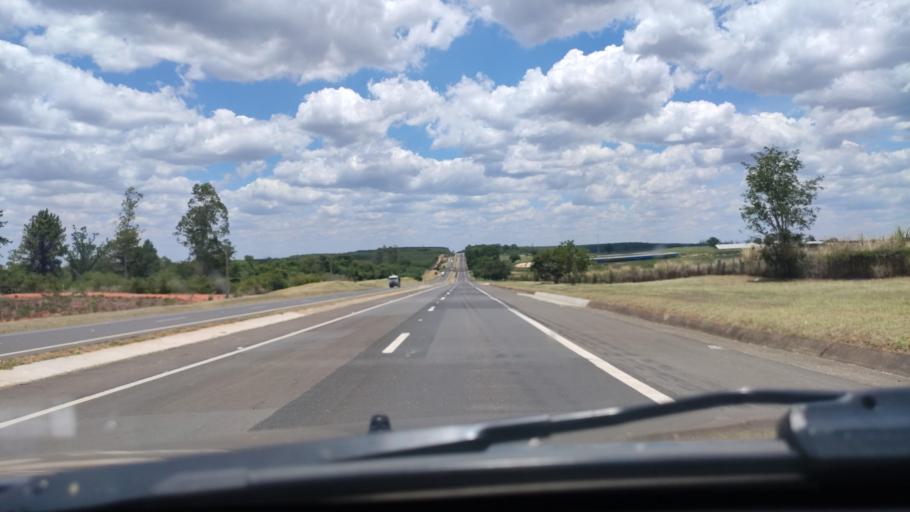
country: BR
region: Sao Paulo
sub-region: Duartina
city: Duartina
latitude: -22.5030
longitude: -49.2814
